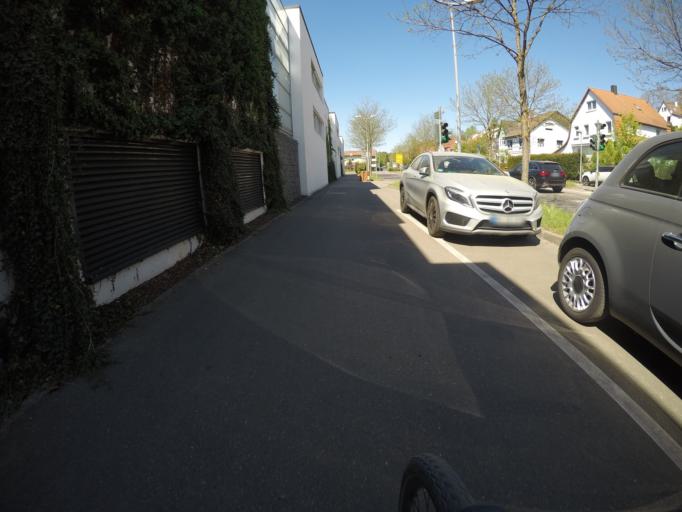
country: DE
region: Baden-Wuerttemberg
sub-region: Regierungsbezirk Stuttgart
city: Waiblingen
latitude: 48.8364
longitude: 9.3160
